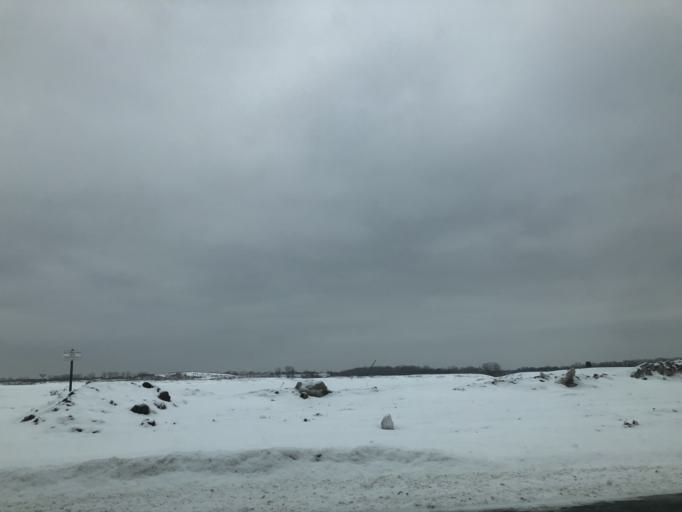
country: US
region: Minnesota
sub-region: Hennepin County
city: Osseo
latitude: 45.0896
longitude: -93.4213
